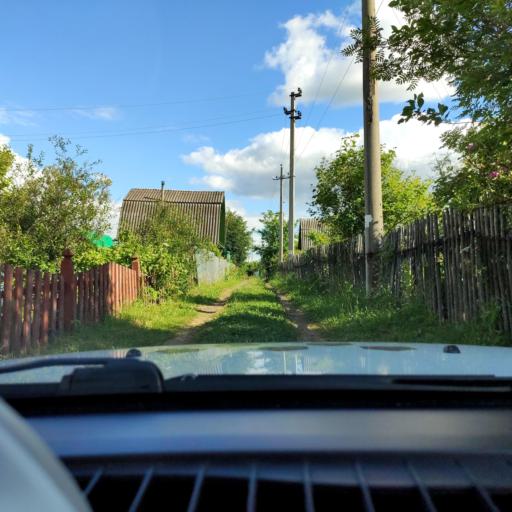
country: RU
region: Perm
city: Overyata
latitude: 58.1056
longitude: 55.8606
